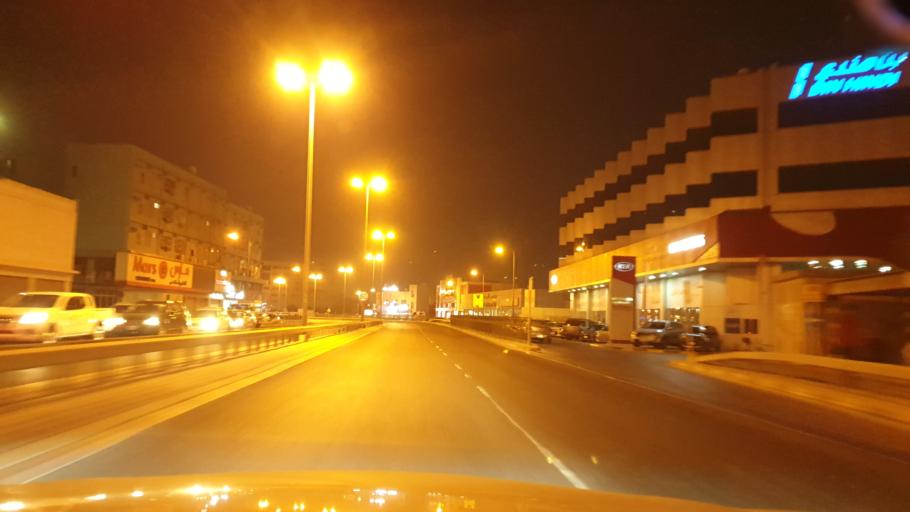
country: BH
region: Manama
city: Jidd Hafs
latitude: 26.2125
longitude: 50.5562
